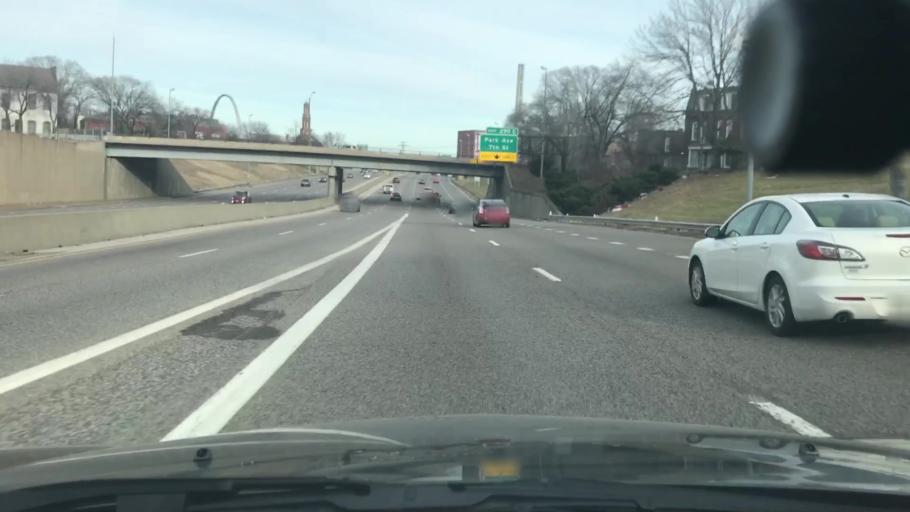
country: US
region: Missouri
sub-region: City of Saint Louis
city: St. Louis
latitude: 38.6107
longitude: -90.2048
